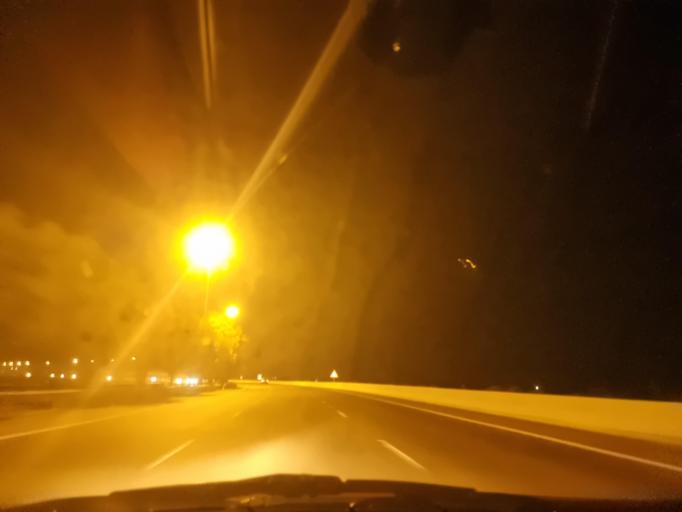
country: AE
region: Abu Dhabi
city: Abu Dhabi
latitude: 24.1850
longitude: 55.0310
